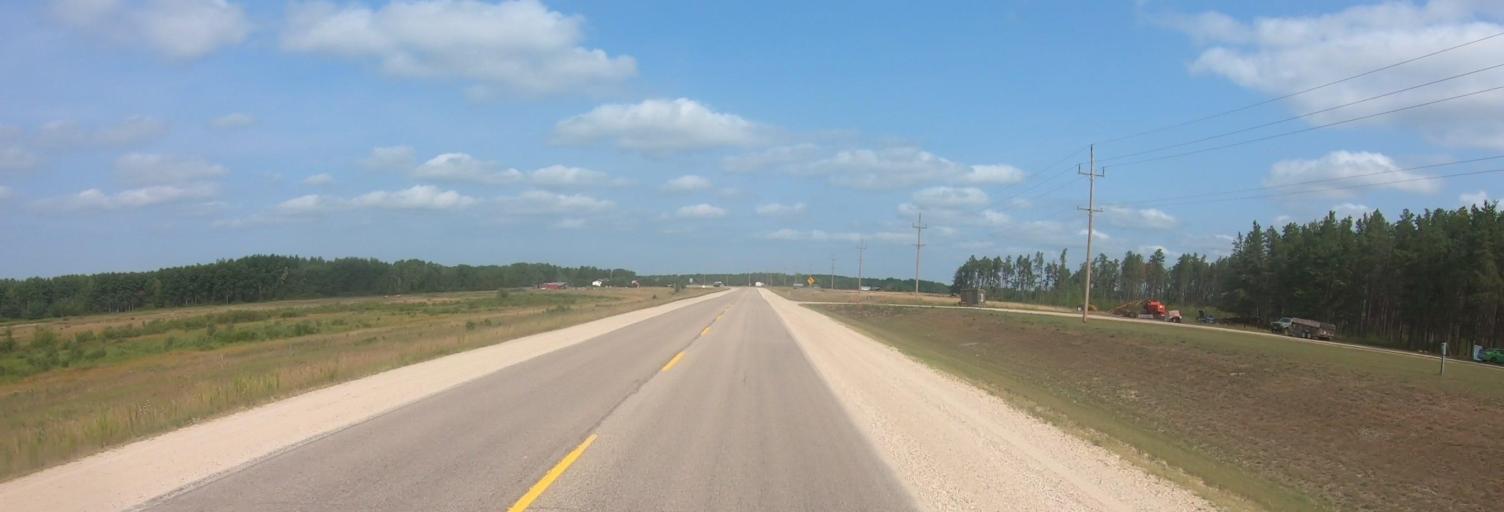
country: CA
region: Manitoba
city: La Broquerie
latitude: 49.2597
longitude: -96.3592
